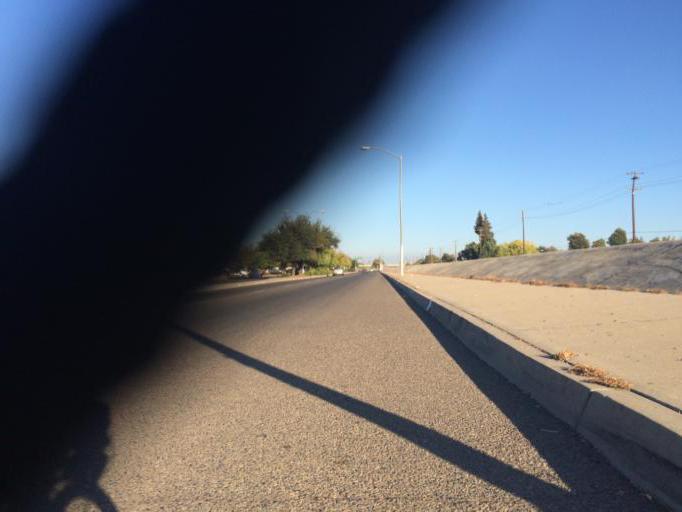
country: US
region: California
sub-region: Fresno County
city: Fresno
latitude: 36.7650
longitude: -119.7591
